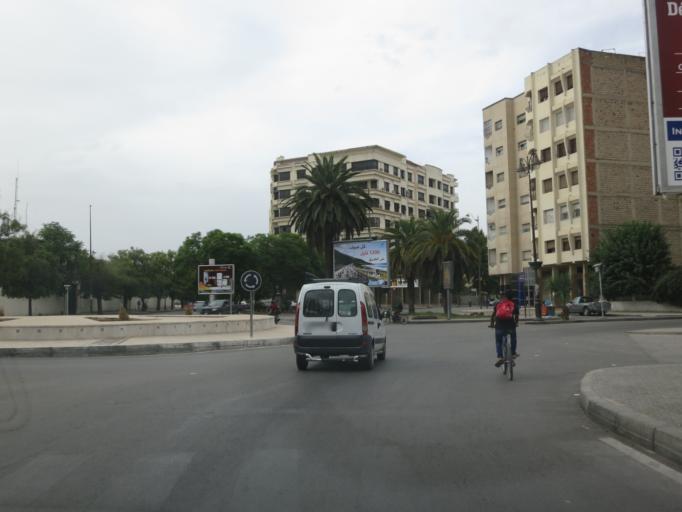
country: MA
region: Fes-Boulemane
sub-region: Fes
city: Fes
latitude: 34.0471
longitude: -5.0016
